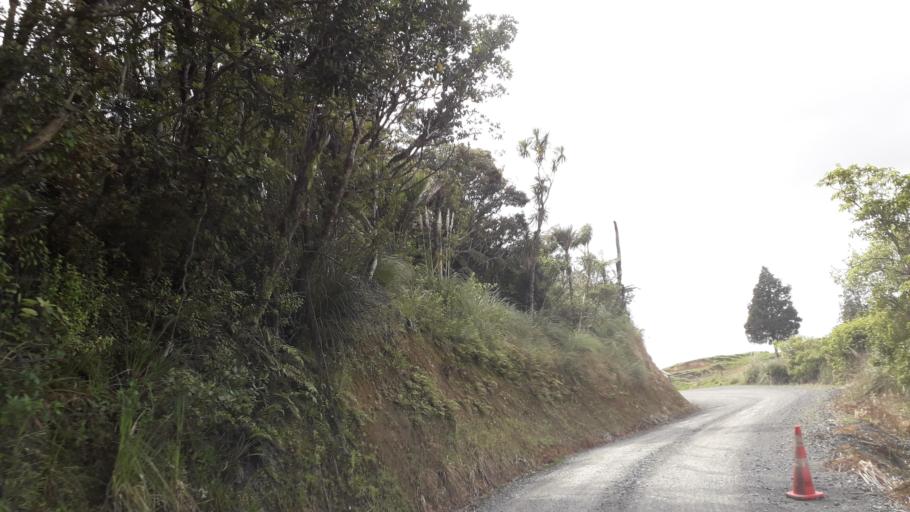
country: NZ
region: Northland
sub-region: Far North District
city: Kaitaia
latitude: -35.1922
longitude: 173.2870
